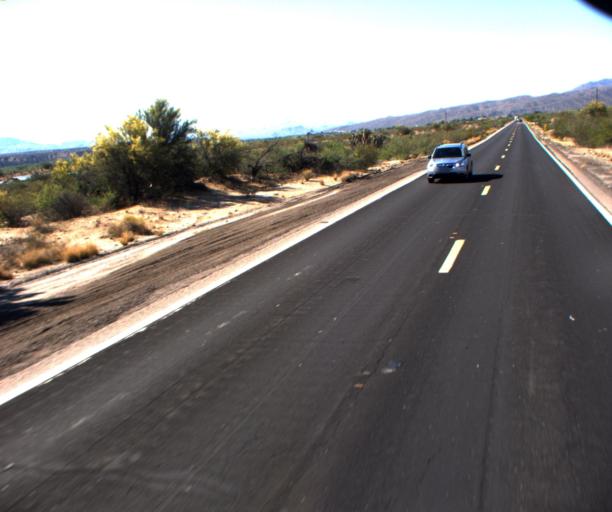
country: US
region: Arizona
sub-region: Yavapai County
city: Bagdad
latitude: 34.7311
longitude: -113.6152
